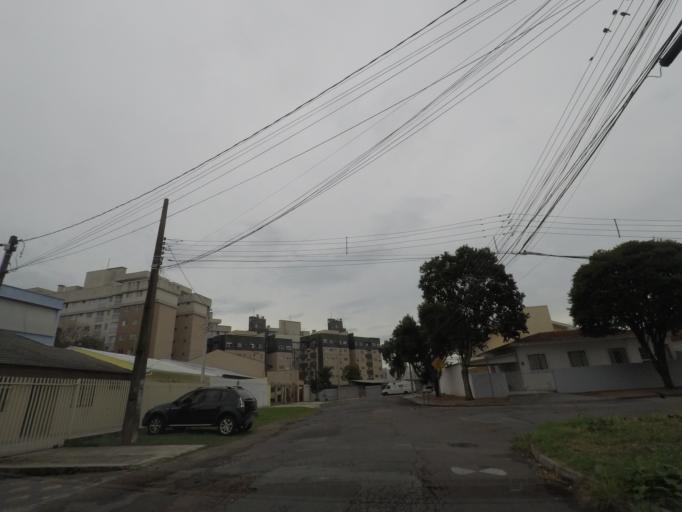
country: BR
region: Parana
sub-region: Curitiba
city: Curitiba
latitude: -25.4730
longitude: -49.2986
